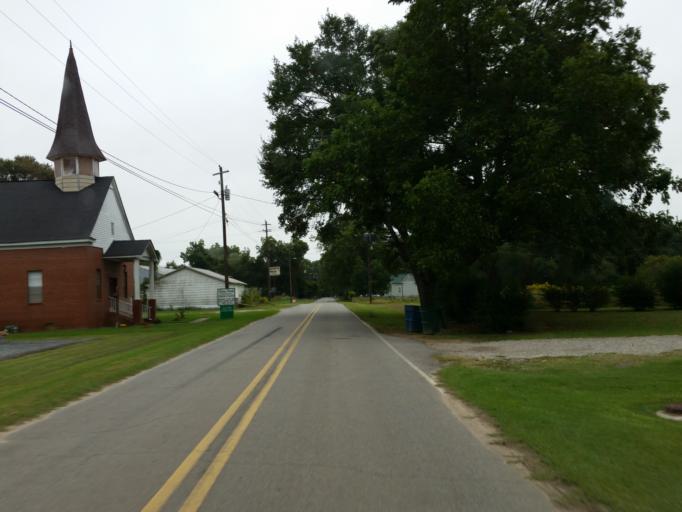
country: US
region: Georgia
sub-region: Dooly County
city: Unadilla
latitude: 32.2674
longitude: -83.7388
